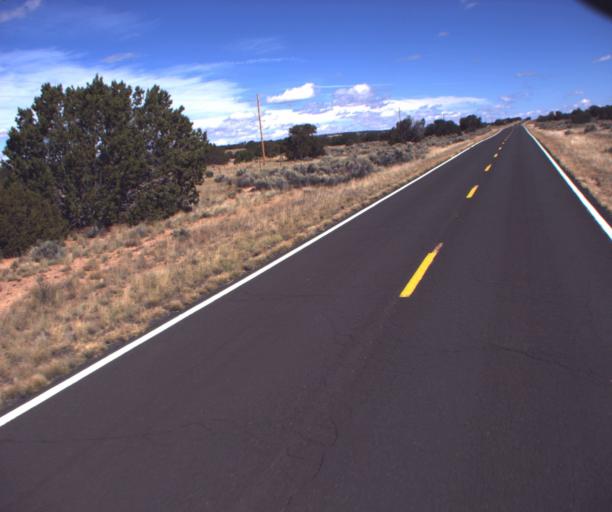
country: US
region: Arizona
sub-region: Apache County
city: Houck
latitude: 34.9164
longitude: -109.2157
